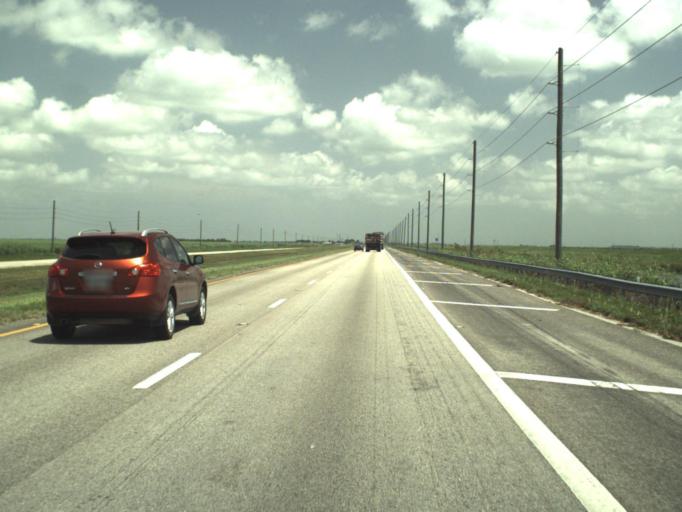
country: US
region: Florida
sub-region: Palm Beach County
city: Belle Glade Camp
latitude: 26.5959
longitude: -80.7111
